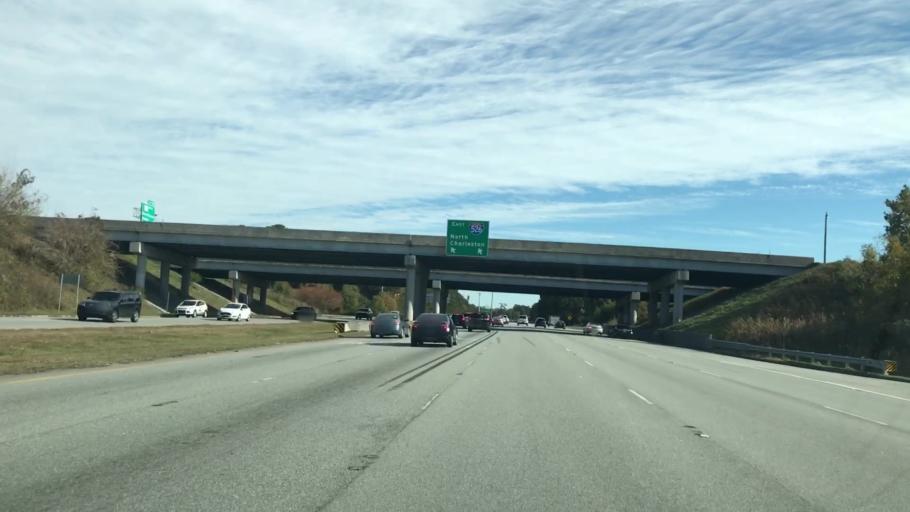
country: US
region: South Carolina
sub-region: Charleston County
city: Shell Point
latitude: 32.8099
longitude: -80.0377
